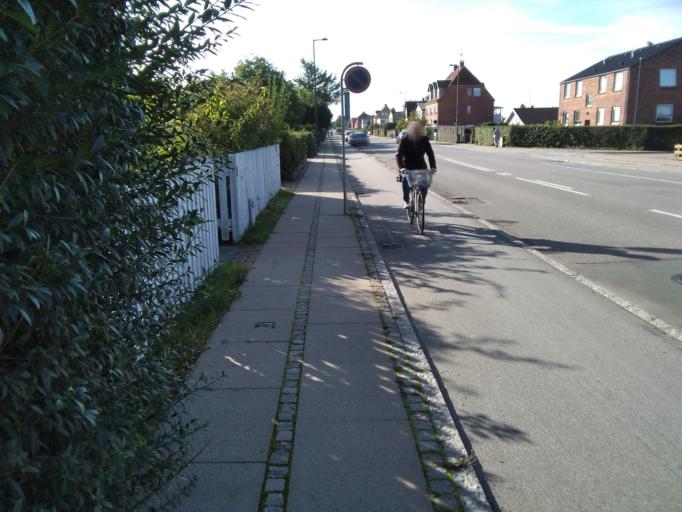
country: DK
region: Capital Region
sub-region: Kobenhavn
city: Vanlose
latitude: 55.7074
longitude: 12.4780
